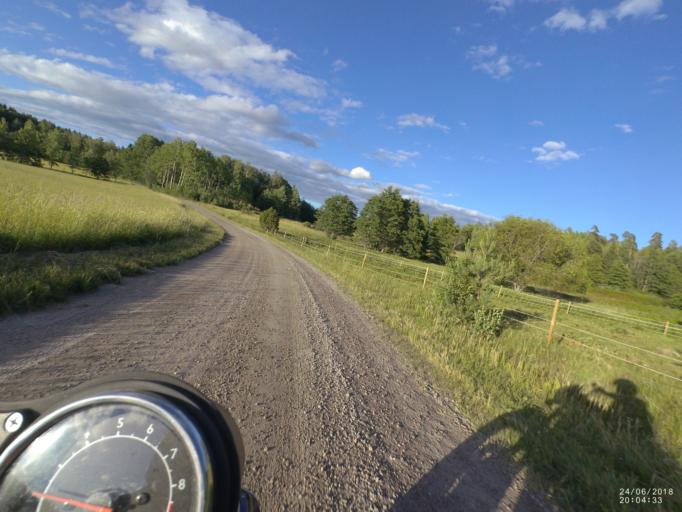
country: SE
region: Soedermanland
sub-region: Nykopings Kommun
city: Nykoping
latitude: 58.8027
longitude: 17.1301
